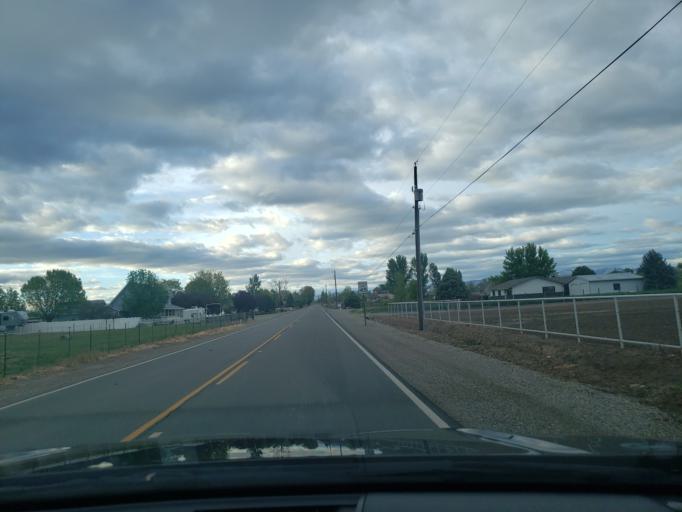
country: US
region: Colorado
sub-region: Mesa County
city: Fruita
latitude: 39.1757
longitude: -108.7291
